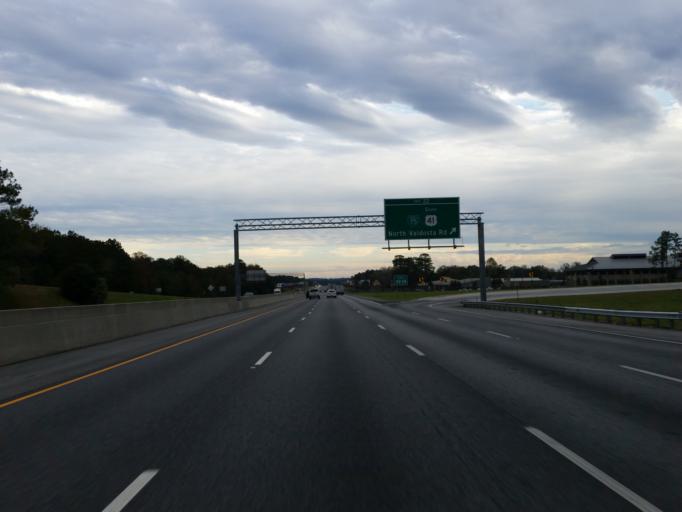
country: US
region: Georgia
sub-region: Lowndes County
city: Remerton
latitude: 30.8943
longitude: -83.3556
